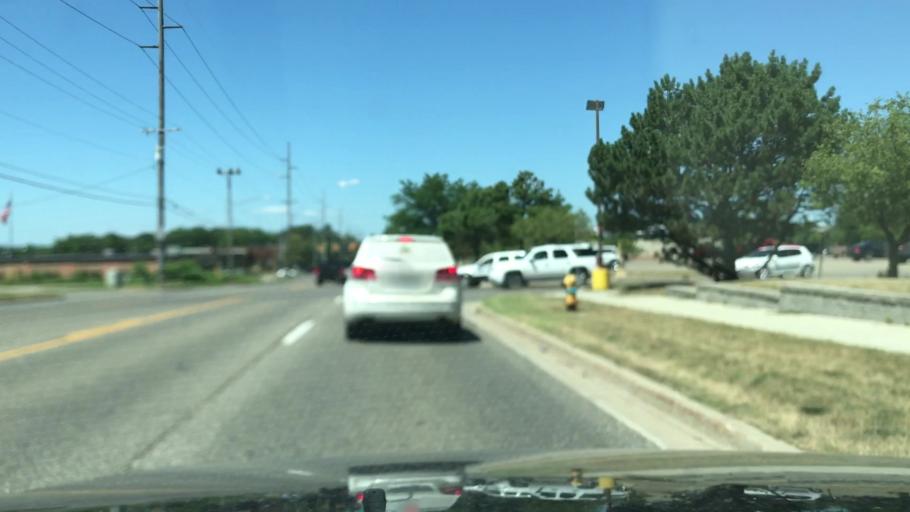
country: US
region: Michigan
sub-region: Ottawa County
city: Holland
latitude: 42.7815
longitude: -86.0774
